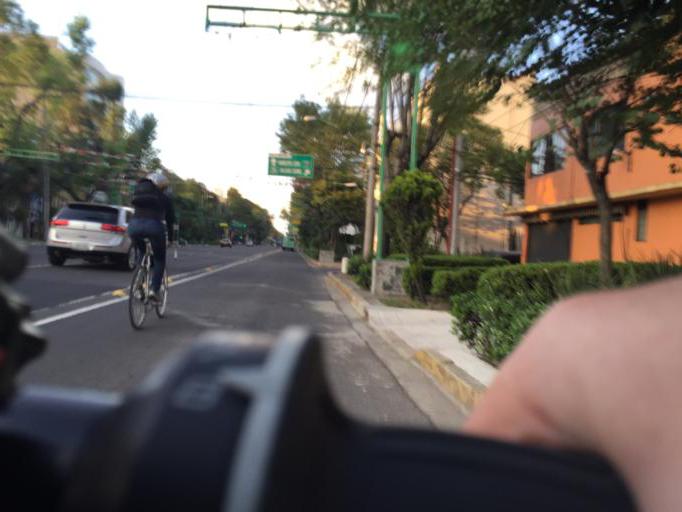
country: MX
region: Mexico City
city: Coyoacan
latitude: 19.3639
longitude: -99.1509
